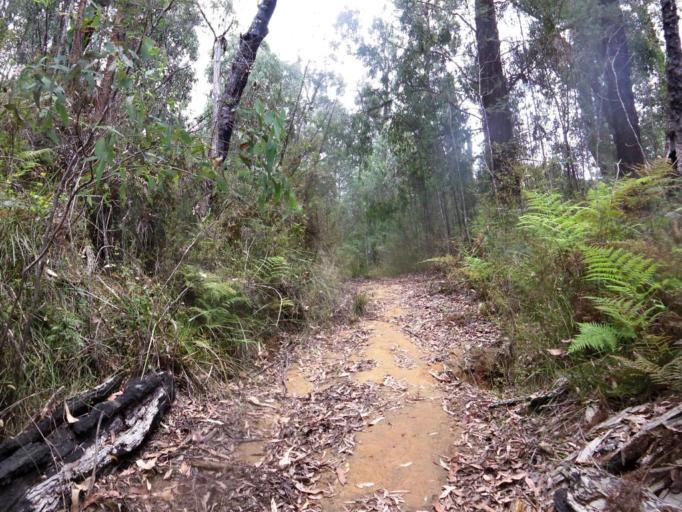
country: AU
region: Victoria
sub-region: Yarra Ranges
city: Healesville
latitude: -37.4508
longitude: 145.5848
